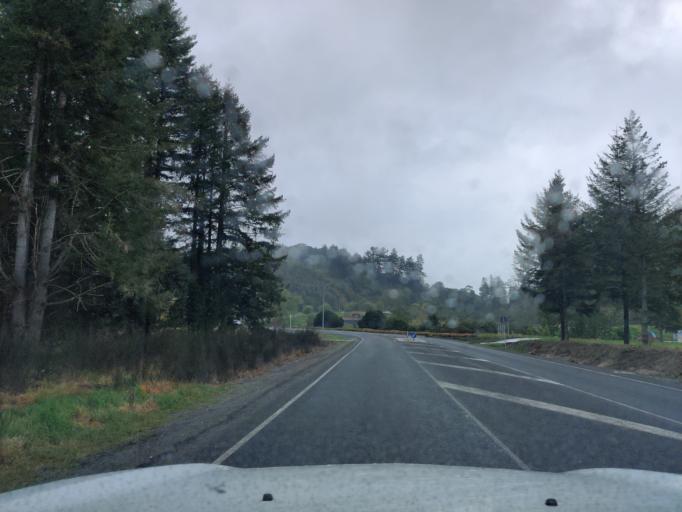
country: NZ
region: Bay of Plenty
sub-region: Rotorua District
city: Rotorua
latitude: -38.1771
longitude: 176.2502
